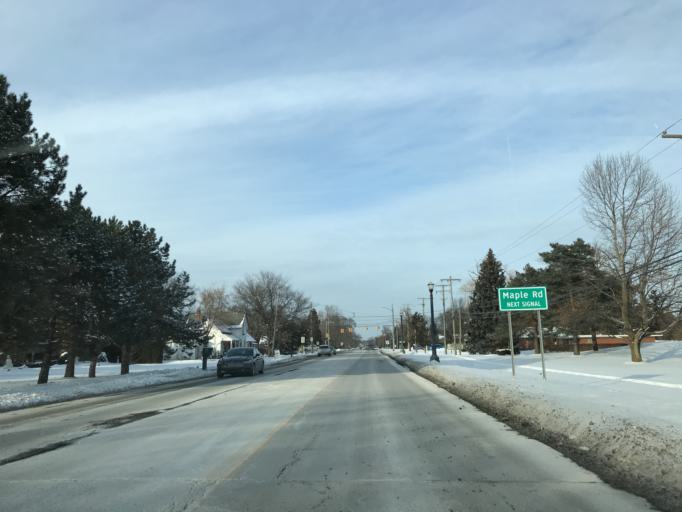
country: US
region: Michigan
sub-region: Oakland County
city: Wixom
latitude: 42.5299
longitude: -83.5363
